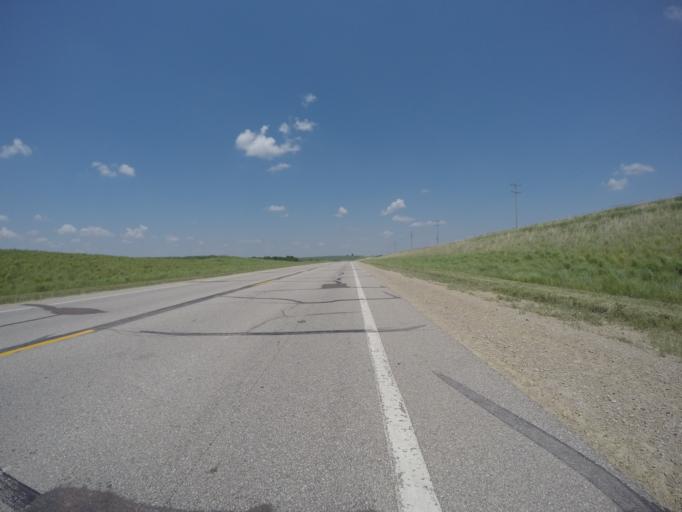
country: US
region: Kansas
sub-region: Doniphan County
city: Troy
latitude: 39.7524
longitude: -95.1438
